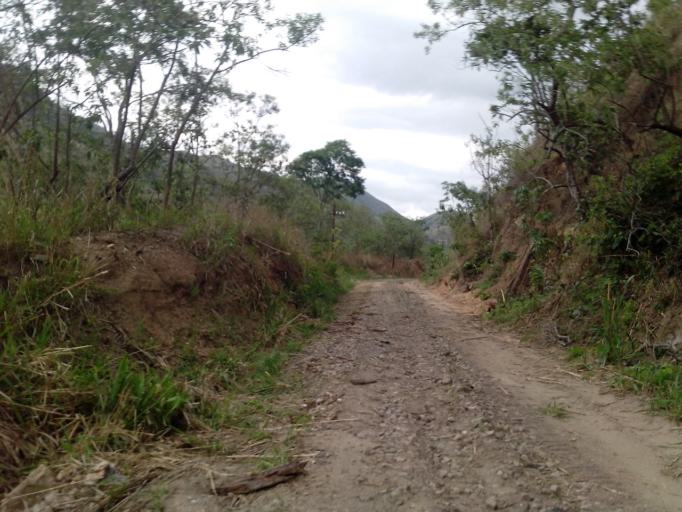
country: BR
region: Rio de Janeiro
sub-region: Miguel Pereira
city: Miguel Pereira
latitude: -22.5054
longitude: -43.5070
